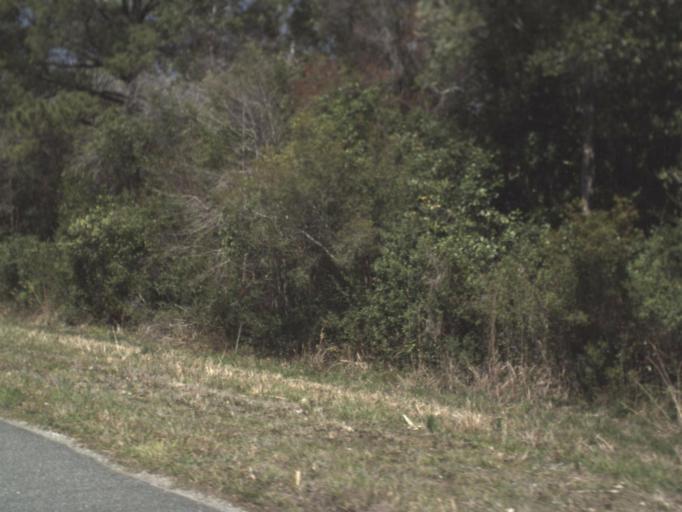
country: US
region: Florida
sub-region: Wakulla County
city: Crawfordville
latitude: 30.3218
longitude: -84.4530
